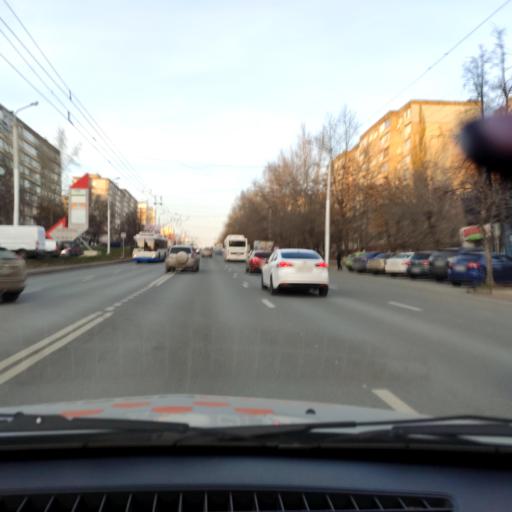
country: RU
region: Bashkortostan
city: Ufa
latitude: 54.7003
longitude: 55.9955
